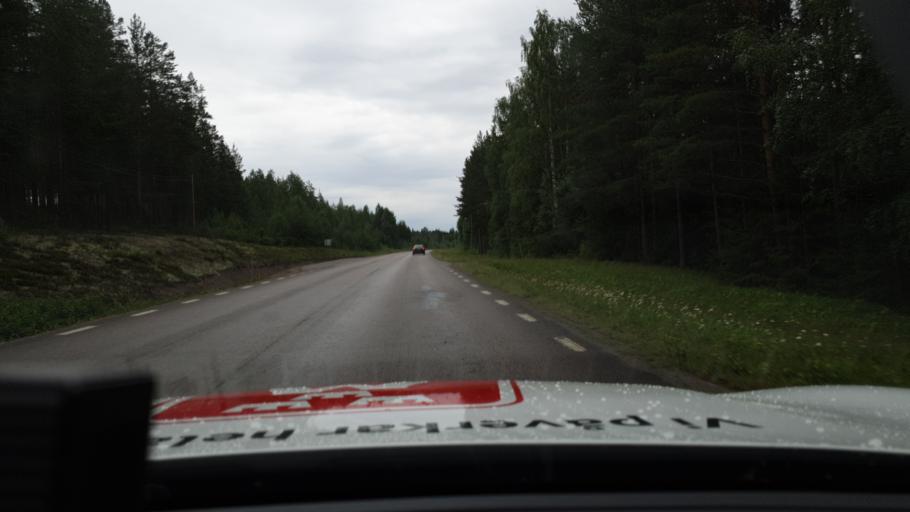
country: SE
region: Norrbotten
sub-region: Alvsbyns Kommun
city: AElvsbyn
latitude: 66.1240
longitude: 20.9180
